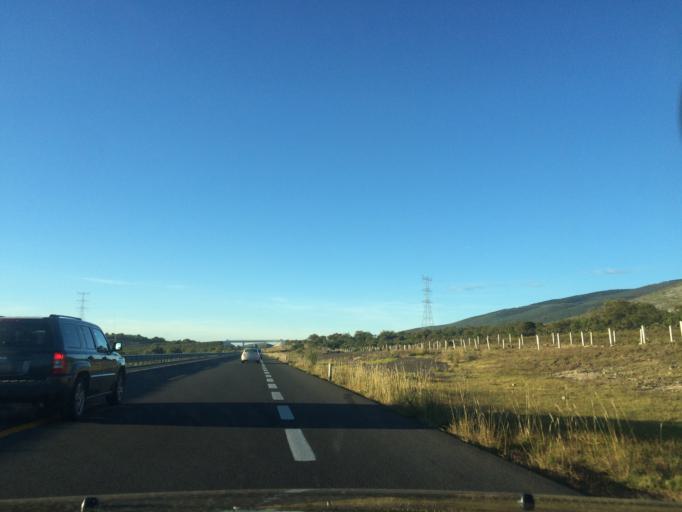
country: MX
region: Puebla
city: Morelos Canada
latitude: 18.7079
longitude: -97.4683
